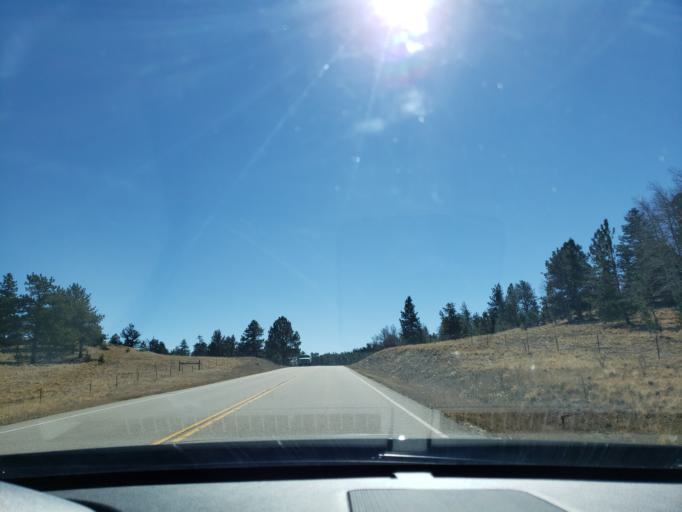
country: US
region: Colorado
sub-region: Chaffee County
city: Buena Vista
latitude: 38.8842
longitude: -105.6807
